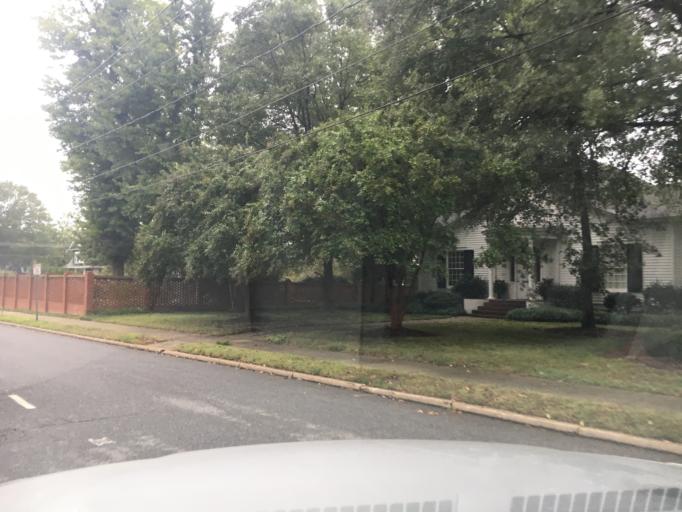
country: US
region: North Carolina
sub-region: Catawba County
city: Hickory
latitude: 35.7356
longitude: -81.3459
